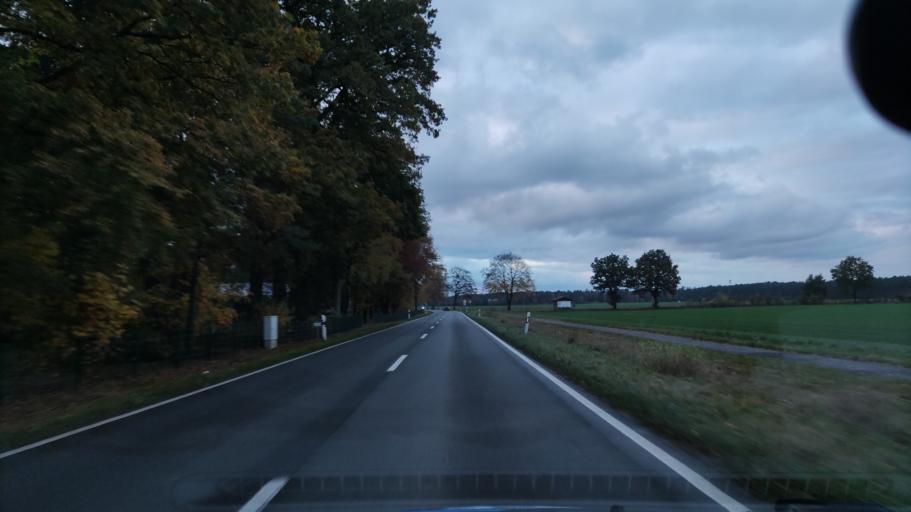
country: DE
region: Lower Saxony
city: Fassberg
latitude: 52.8814
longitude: 10.1901
